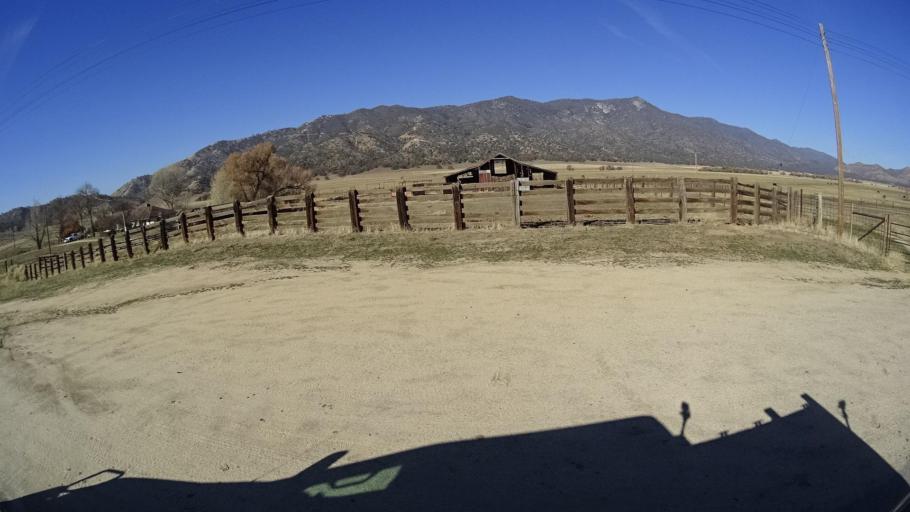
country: US
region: California
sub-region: Kern County
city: Bodfish
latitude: 35.3890
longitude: -118.5345
